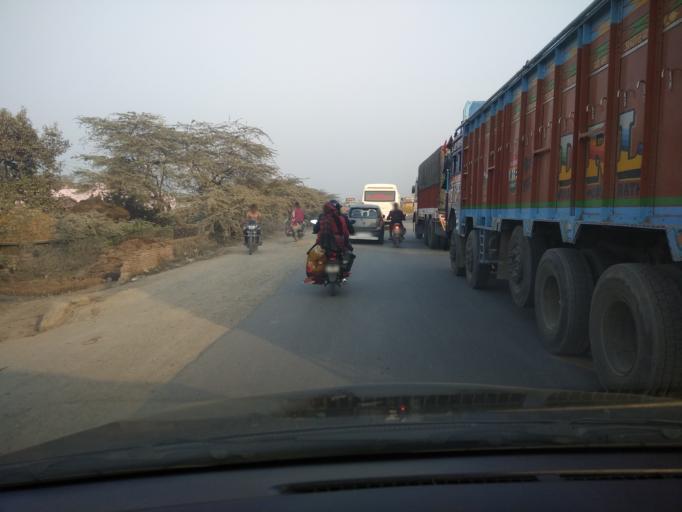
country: IN
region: Uttar Pradesh
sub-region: Varanasi
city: Ramnagar
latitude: 25.2521
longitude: 83.0654
